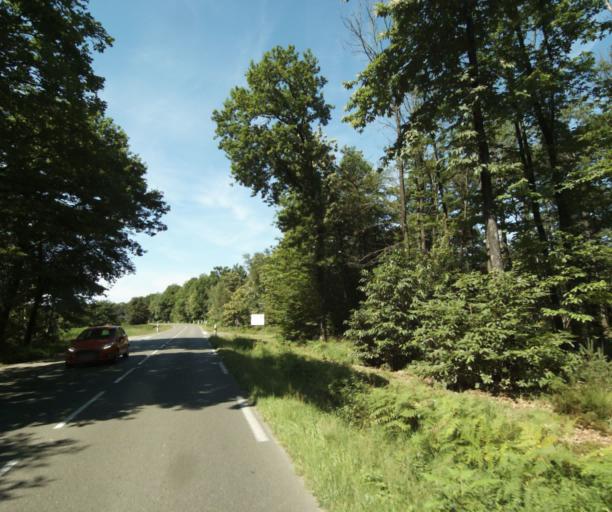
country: FR
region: Pays de la Loire
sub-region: Departement de la Mayenne
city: Laval
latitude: 48.0420
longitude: -0.7776
